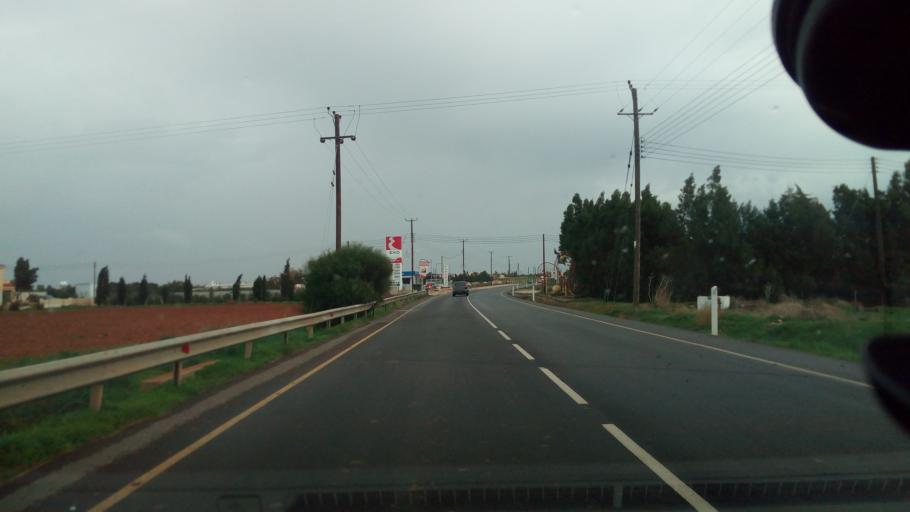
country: CY
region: Ammochostos
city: Deryneia
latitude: 35.0543
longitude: 33.9418
